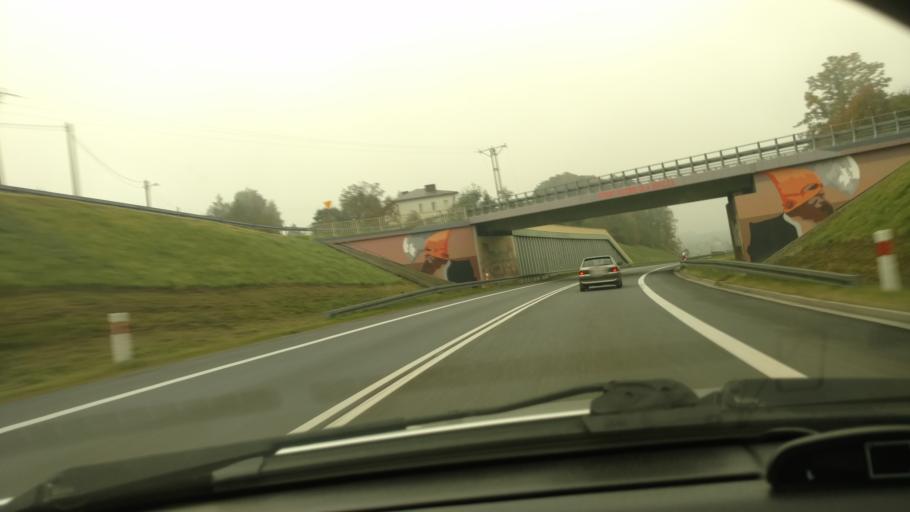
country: PL
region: Lesser Poland Voivodeship
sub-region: Powiat gorlicki
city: Biecz
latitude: 49.7139
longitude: 21.2503
